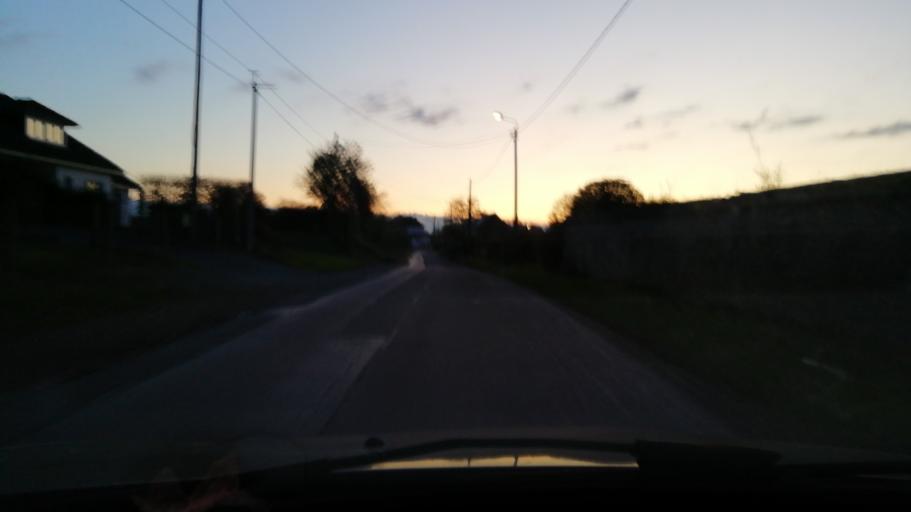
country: FR
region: Nord-Pas-de-Calais
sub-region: Departement du Nord
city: Marpent
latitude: 50.2651
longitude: 4.0870
